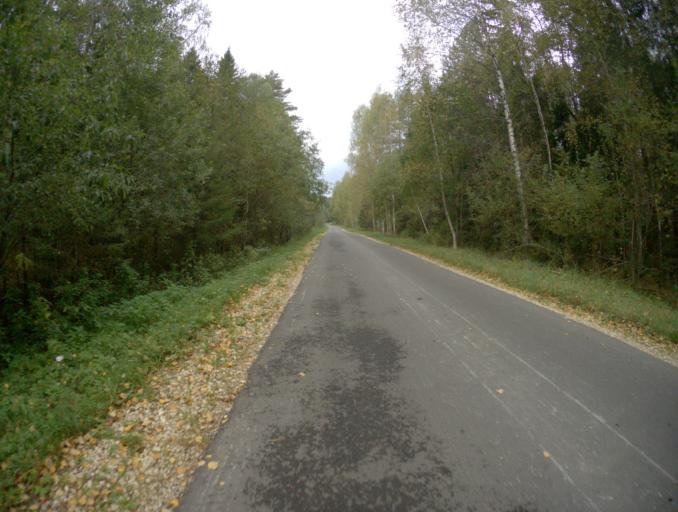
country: RU
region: Vladimir
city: Kideksha
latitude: 56.4730
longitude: 40.6572
